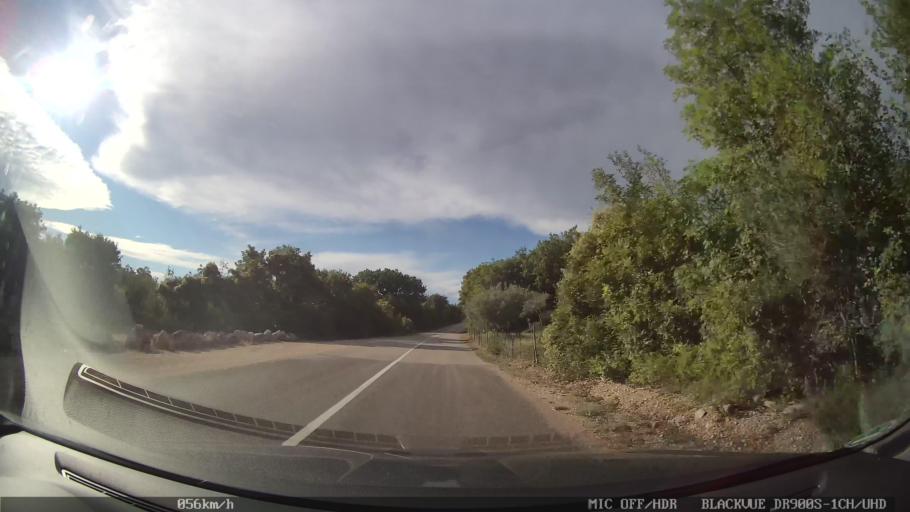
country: HR
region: Primorsko-Goranska
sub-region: Grad Krk
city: Krk
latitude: 45.0636
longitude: 14.4756
